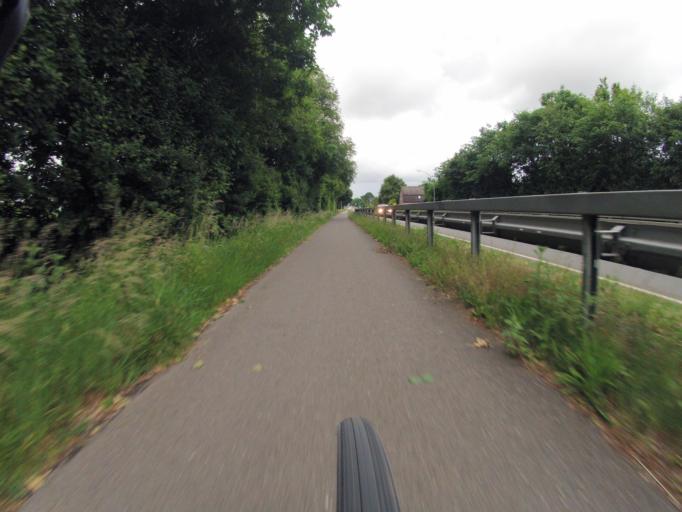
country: DE
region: North Rhine-Westphalia
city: Emsdetten
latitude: 52.1849
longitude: 7.5455
